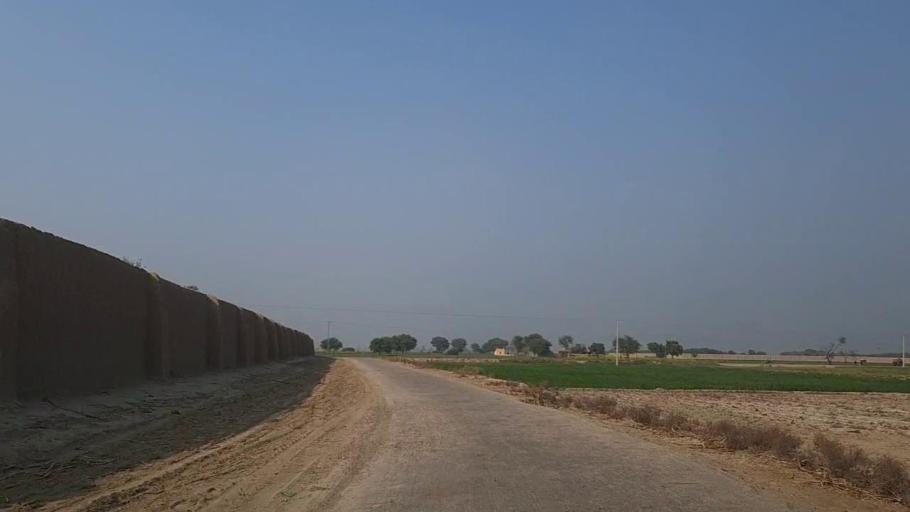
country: PK
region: Sindh
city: Sann
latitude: 26.1093
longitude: 68.1758
